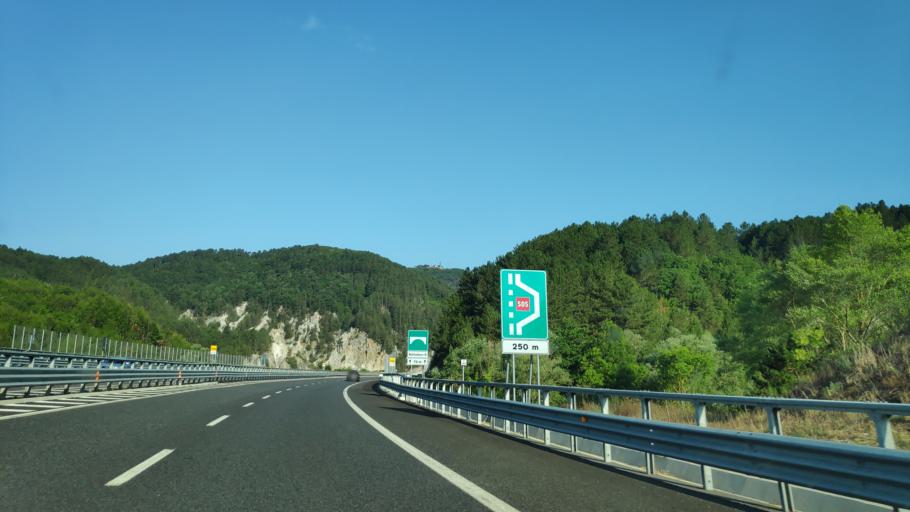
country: IT
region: Calabria
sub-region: Provincia di Cosenza
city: Mormanno
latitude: 39.8773
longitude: 15.9926
